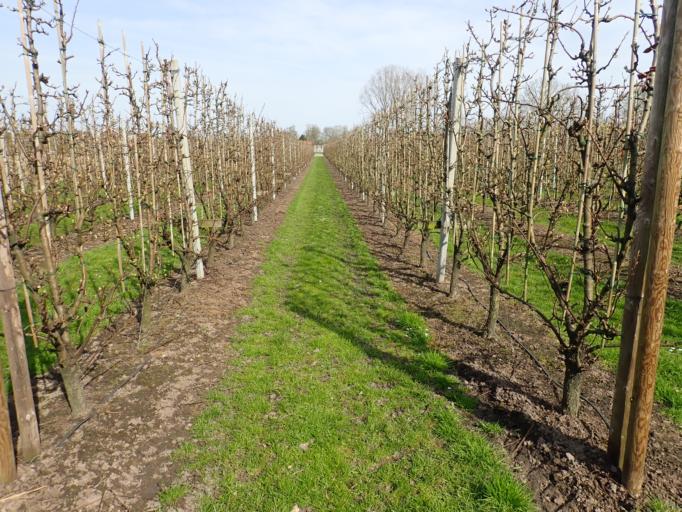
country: BE
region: Flanders
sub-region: Provincie Antwerpen
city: Ranst
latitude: 51.1663
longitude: 4.6060
